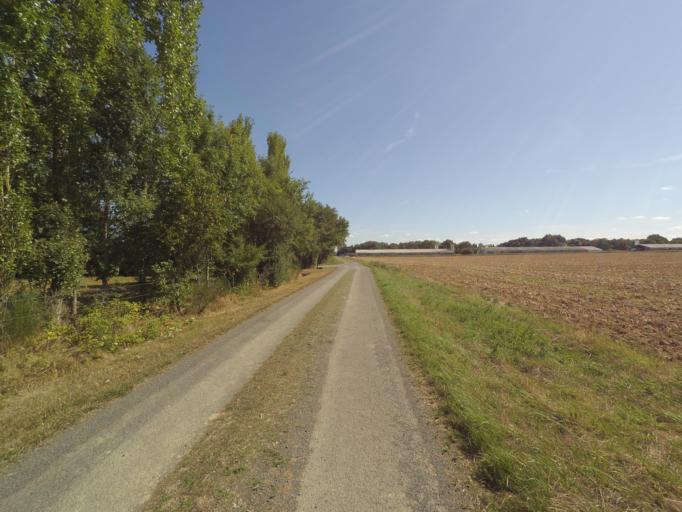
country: FR
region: Pays de la Loire
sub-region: Departement de la Vendee
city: Saint-Andre-Treize-Voies
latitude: 46.9532
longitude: -1.4125
